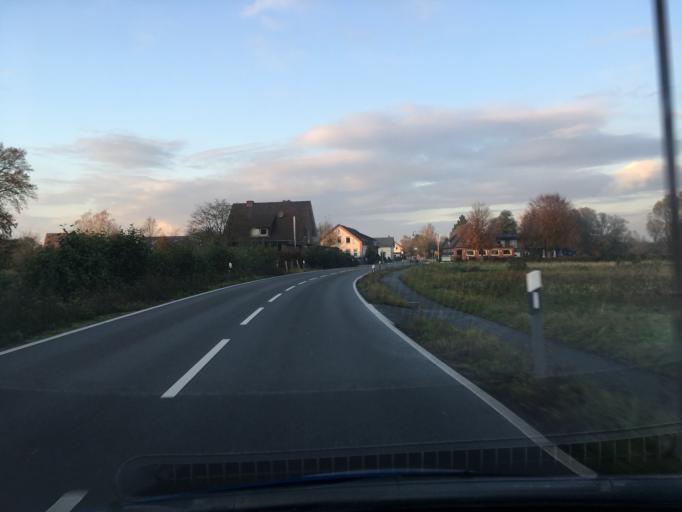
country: DE
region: Lower Saxony
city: Bardowick
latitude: 53.3105
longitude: 10.3868
